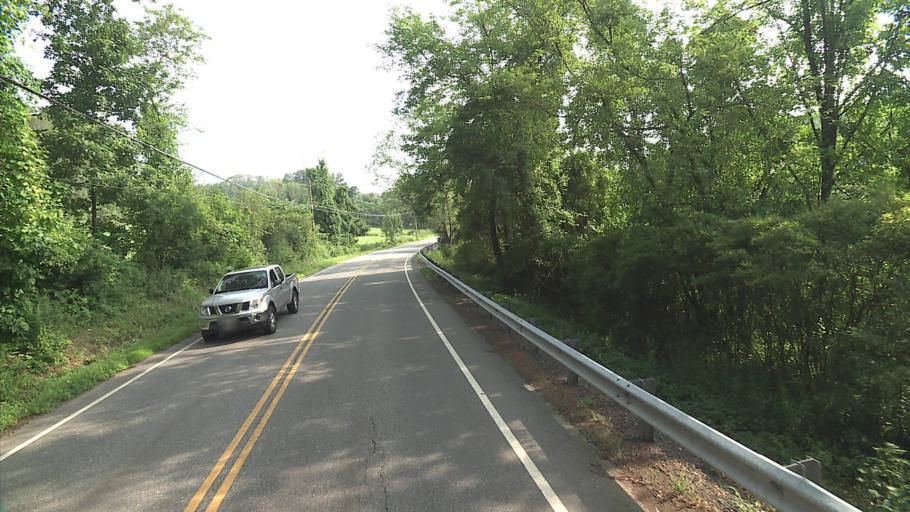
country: US
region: Connecticut
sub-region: Windham County
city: Quinebaug
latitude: 42.0132
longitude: -71.9658
